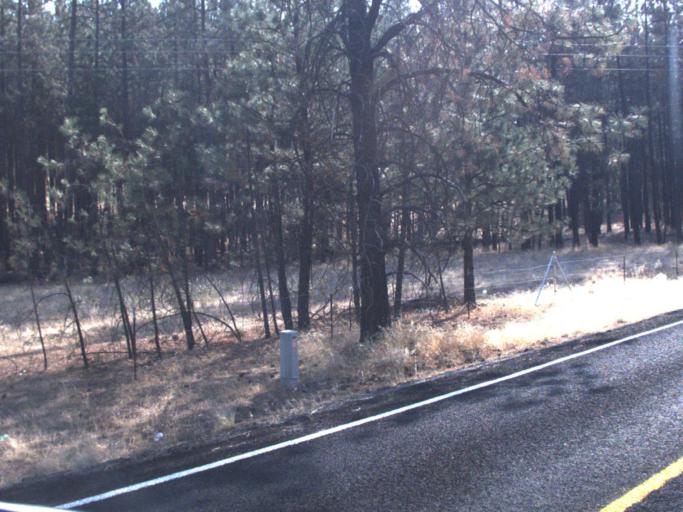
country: US
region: Washington
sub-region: Spokane County
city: Fairchild Air Force Base
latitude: 47.8453
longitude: -117.8497
